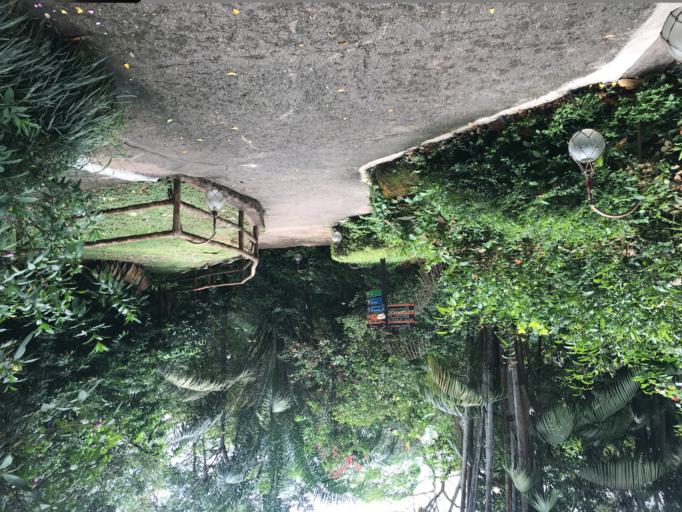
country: MY
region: Johor
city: Johor Bahru
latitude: 1.4050
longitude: 103.7941
